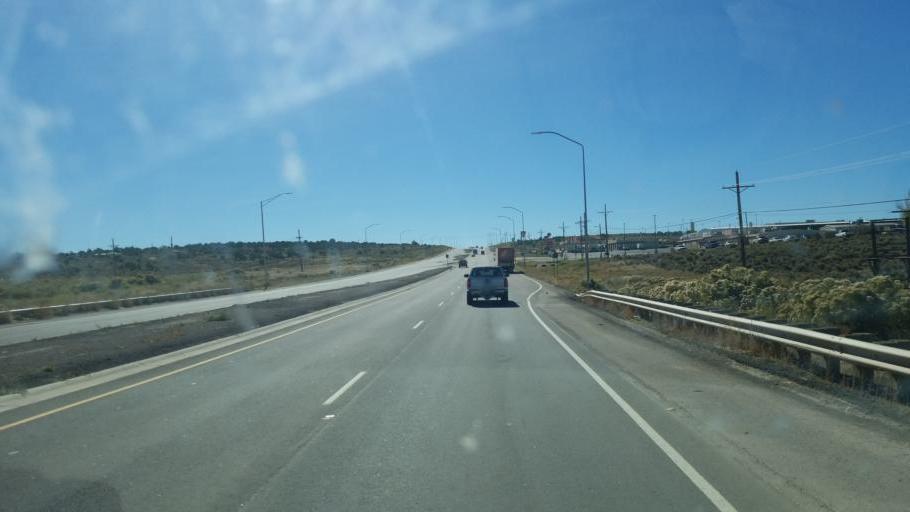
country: US
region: New Mexico
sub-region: McKinley County
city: Gallup
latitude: 35.6102
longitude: -108.7775
